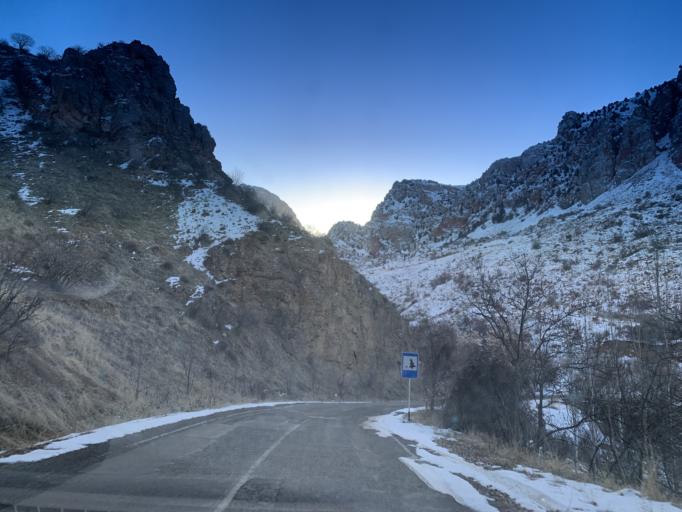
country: AM
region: Vayots' Dzori Marz
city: Areni
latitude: 39.6831
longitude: 45.2342
